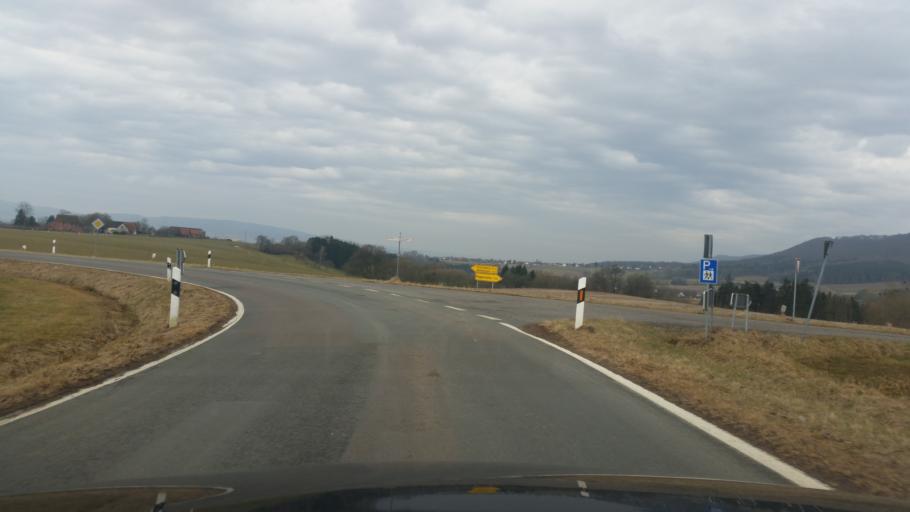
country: DE
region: Lower Saxony
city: Hessisch Oldendorf
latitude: 52.1810
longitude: 9.3144
